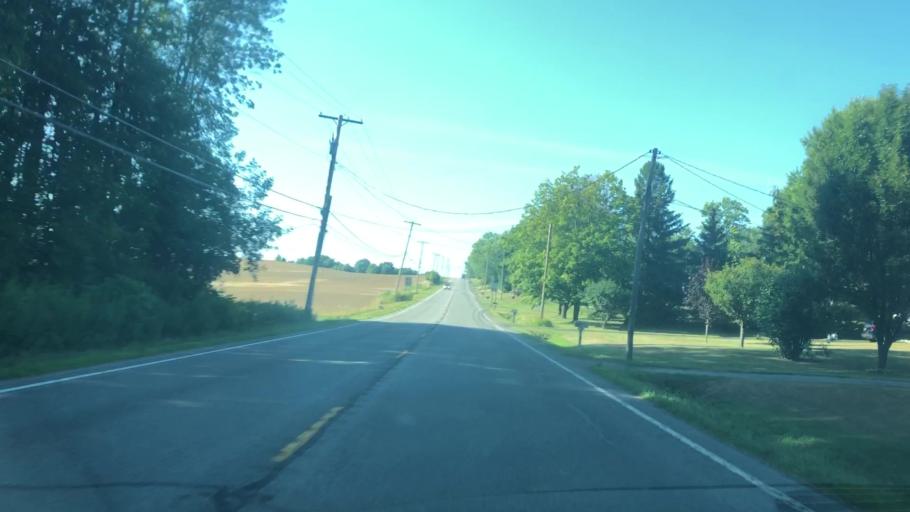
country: US
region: New York
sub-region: Wayne County
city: Macedon
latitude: 43.1321
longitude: -77.2926
